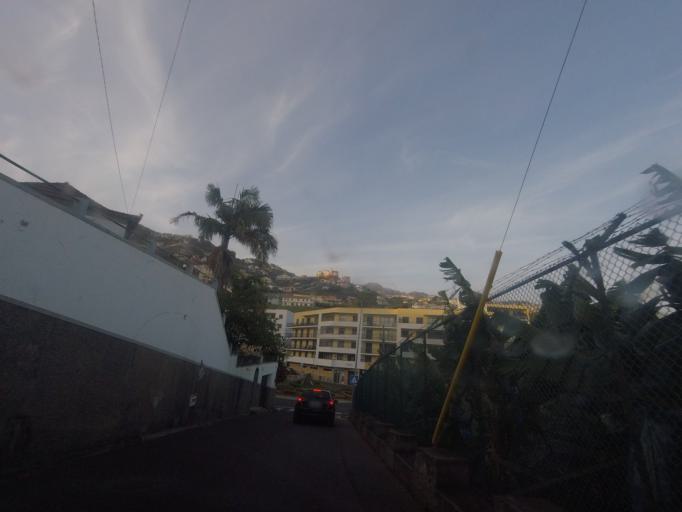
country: PT
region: Madeira
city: Camara de Lobos
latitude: 32.6528
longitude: -16.9846
